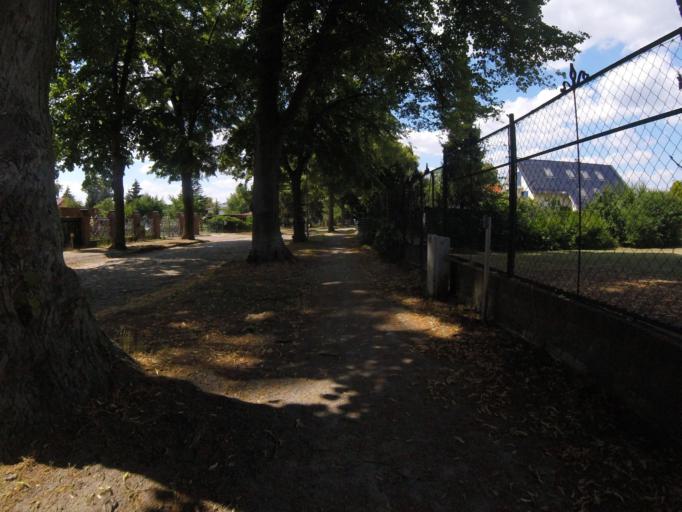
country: DE
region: Brandenburg
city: Wildau
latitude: 52.3364
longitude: 13.6445
